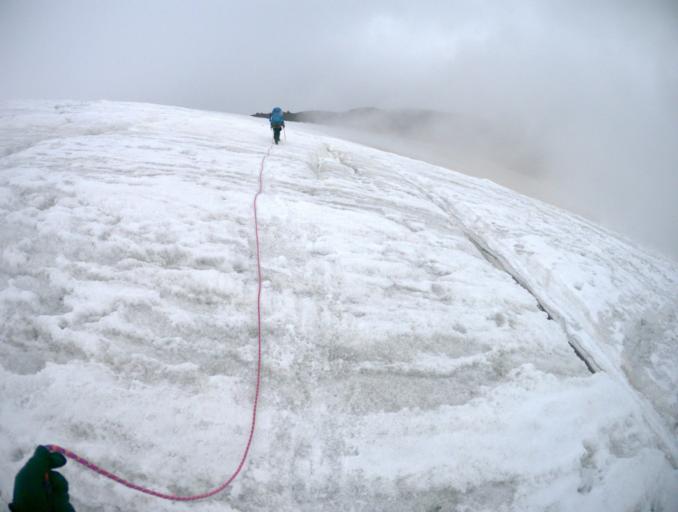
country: RU
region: Kabardino-Balkariya
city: Terskol
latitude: 43.3681
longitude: 42.4955
